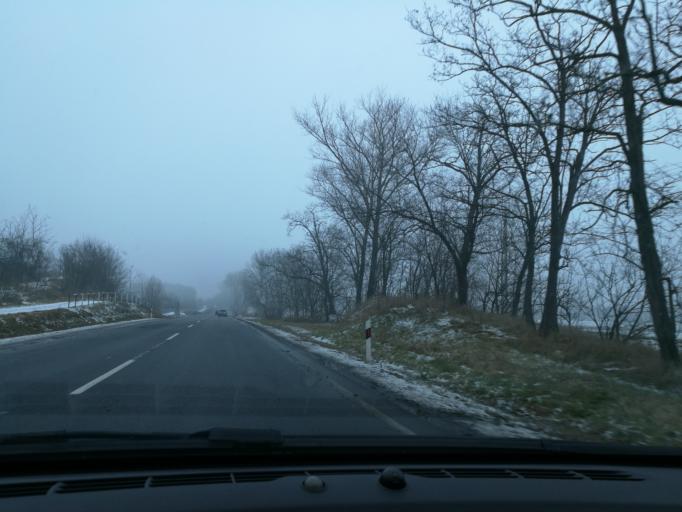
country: HU
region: Szabolcs-Szatmar-Bereg
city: Nyirpazony
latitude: 47.9969
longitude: 21.8112
